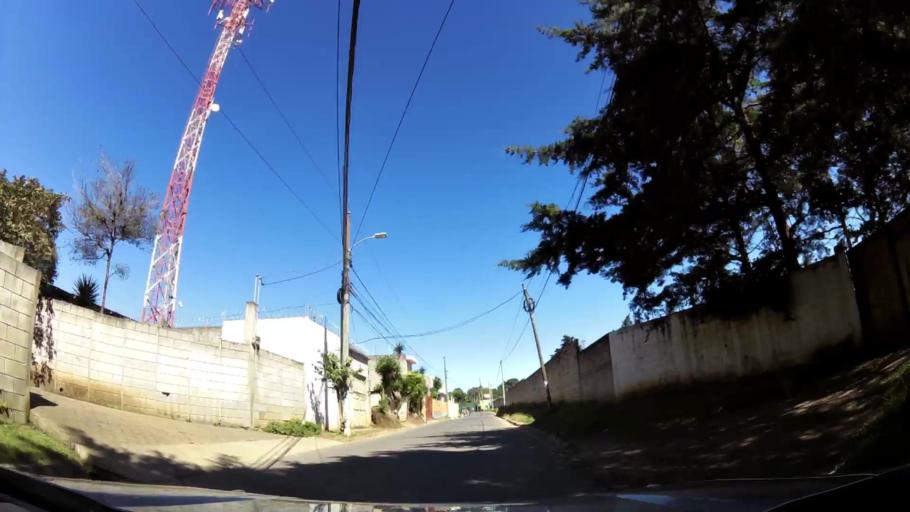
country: GT
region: Guatemala
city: San Jose Pinula
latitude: 14.5266
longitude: -90.4153
